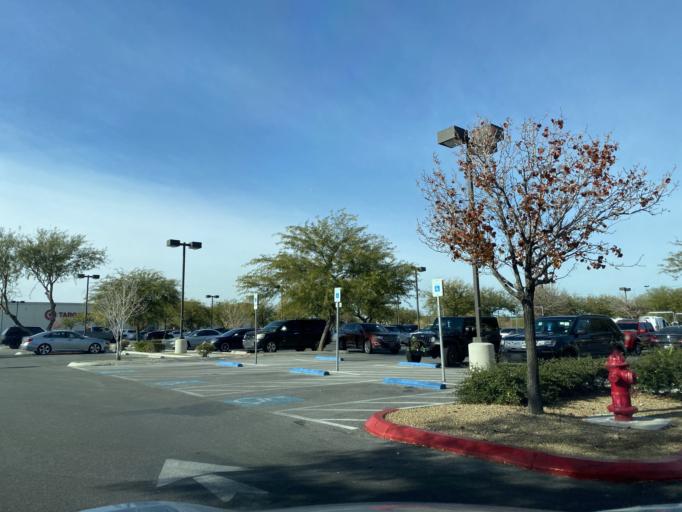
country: US
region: Nevada
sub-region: Clark County
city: Las Vegas
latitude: 36.2799
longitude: -115.2620
